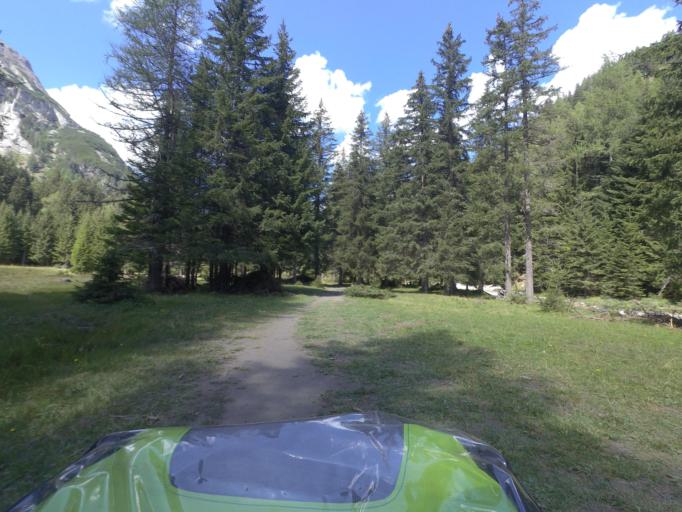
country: AT
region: Salzburg
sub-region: Politischer Bezirk Tamsweg
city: Zederhaus
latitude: 47.1847
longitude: 13.3899
